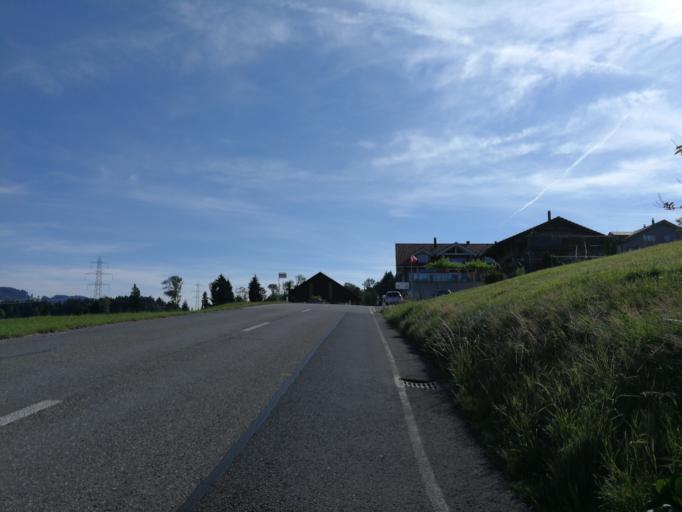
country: CH
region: Saint Gallen
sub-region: Wahlkreis See-Gaster
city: Gommiswald
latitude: 47.2502
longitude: 9.0298
